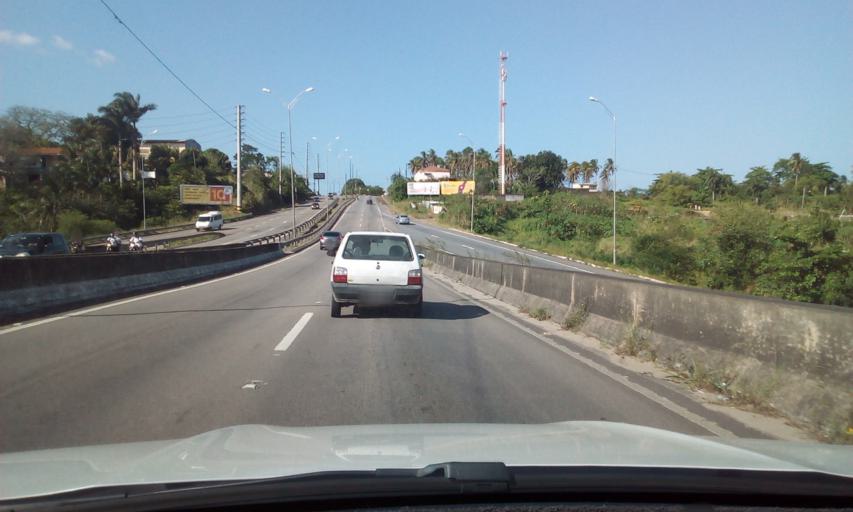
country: BR
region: Paraiba
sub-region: Bayeux
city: Bayeux
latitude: -7.1495
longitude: -34.9105
